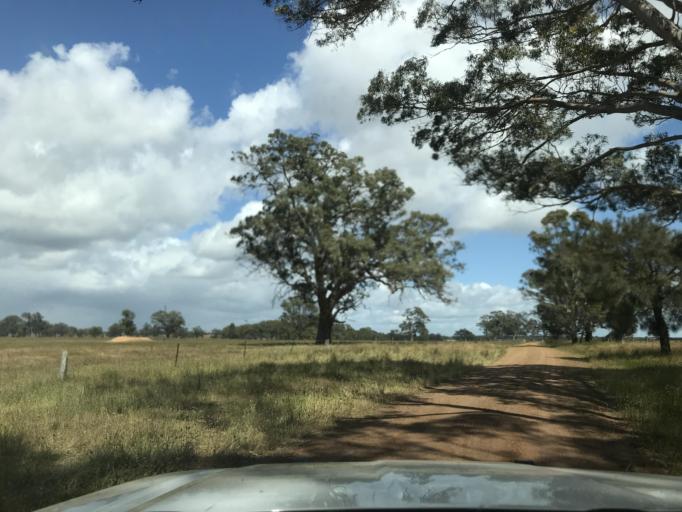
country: AU
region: South Australia
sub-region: Wattle Range
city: Penola
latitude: -37.2012
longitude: 141.4177
